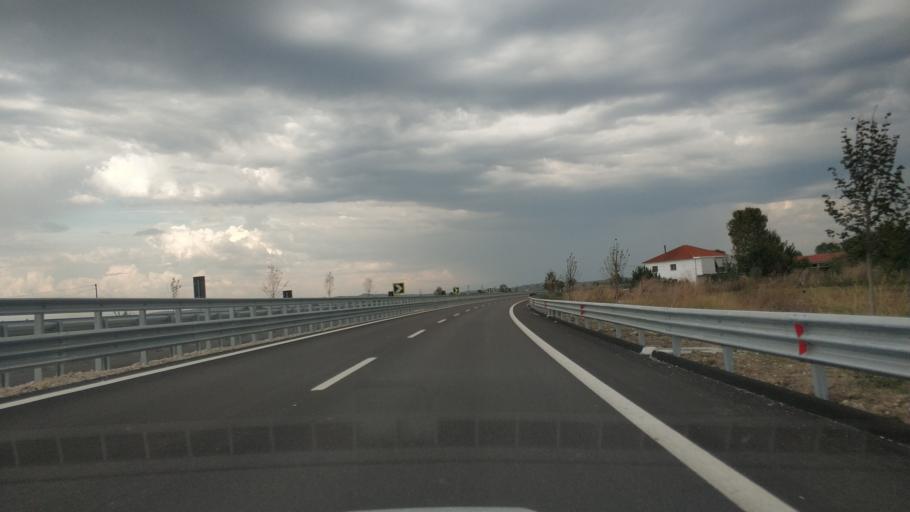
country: AL
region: Fier
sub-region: Rrethi i Fierit
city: Dermenas
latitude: 40.7485
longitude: 19.5116
